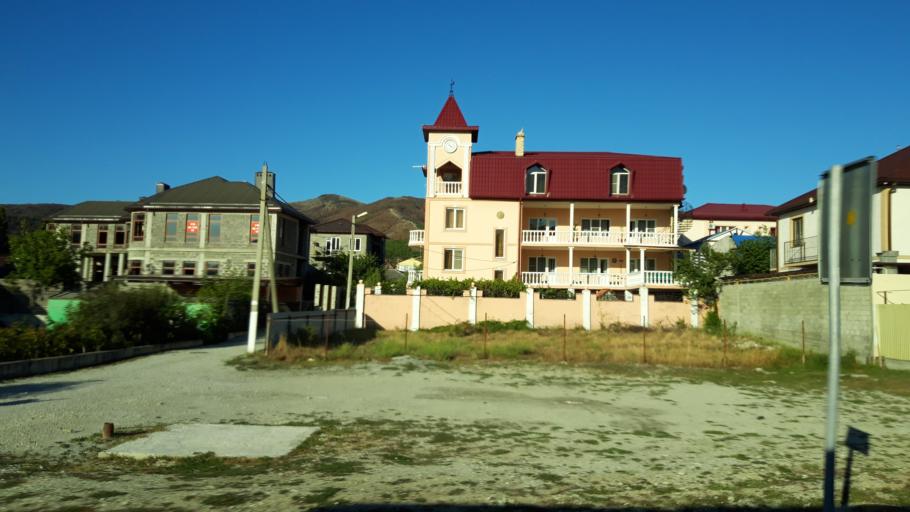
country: RU
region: Krasnodarskiy
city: Kabardinka
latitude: 44.6471
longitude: 37.9522
